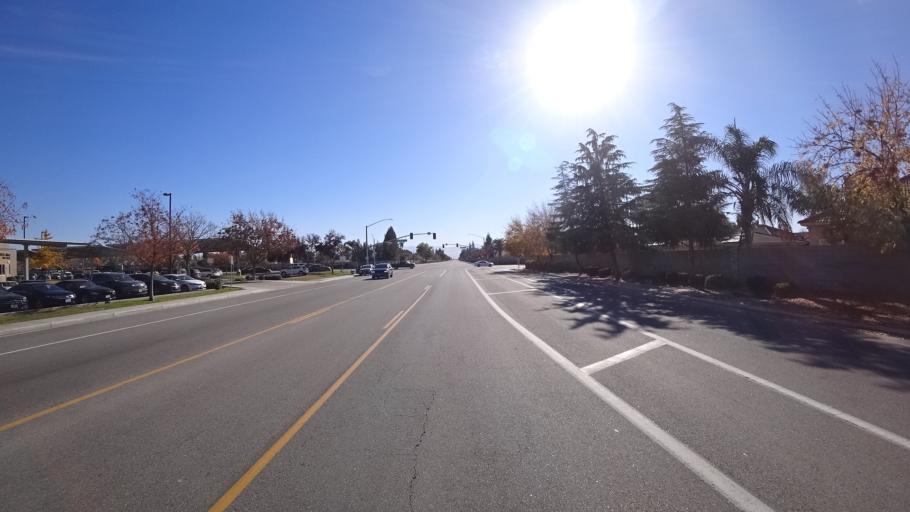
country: US
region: California
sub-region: Kern County
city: Greenfield
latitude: 35.2823
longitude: -119.0479
